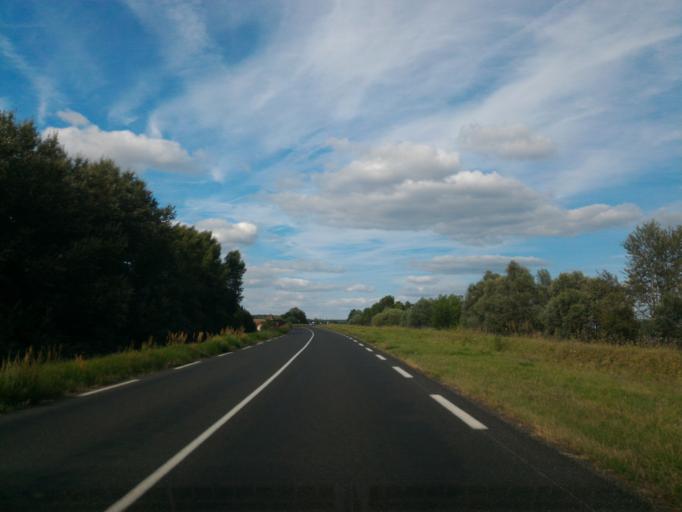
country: FR
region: Centre
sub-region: Departement d'Indre-et-Loire
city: Cangey
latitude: 47.4590
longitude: 1.0784
